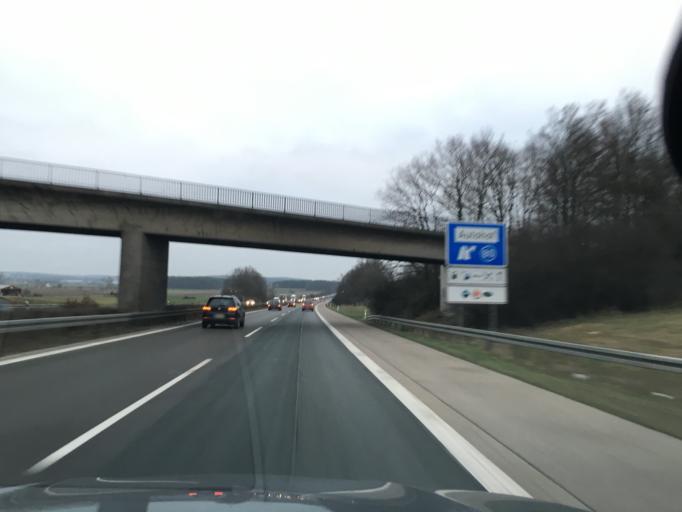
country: DE
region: Bavaria
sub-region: Regierungsbezirk Mittelfranken
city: Gremsdorf
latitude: 49.6838
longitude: 10.8638
